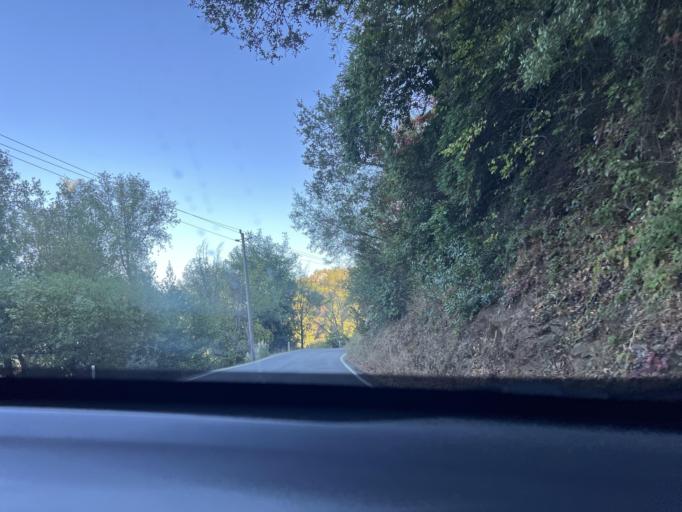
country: US
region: California
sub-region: Santa Clara County
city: Loyola
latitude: 37.2943
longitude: -122.1032
